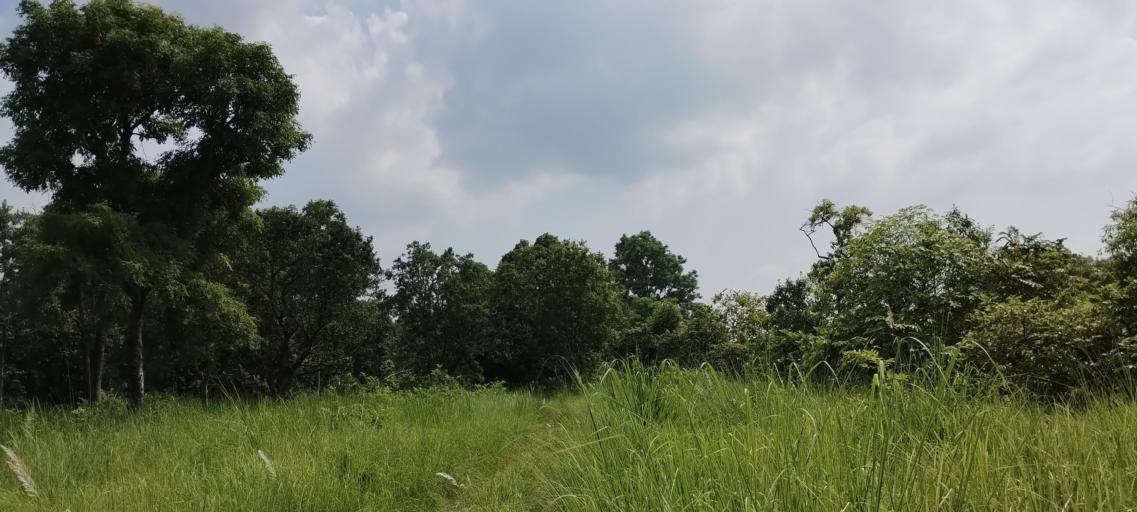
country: NP
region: Far Western
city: Tikapur
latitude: 28.5084
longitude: 81.2477
